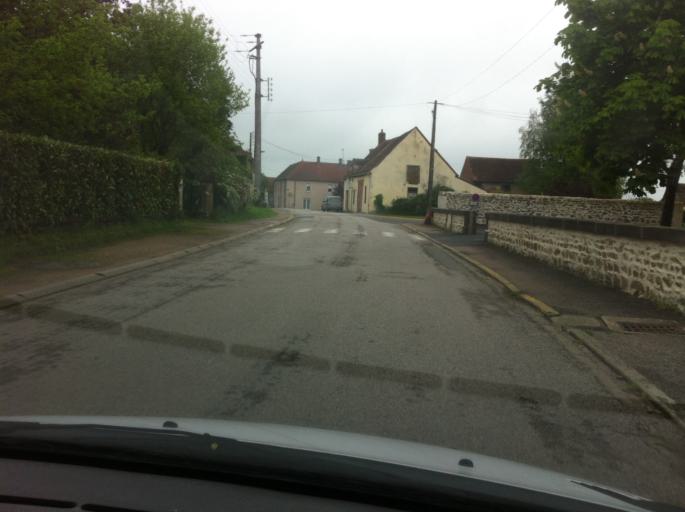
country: FR
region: Auvergne
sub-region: Departement de l'Allier
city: Montmarault
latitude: 46.3265
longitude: 3.0630
